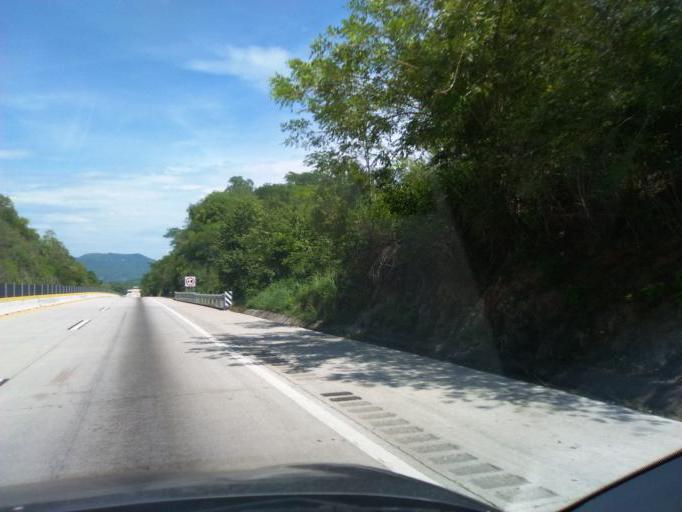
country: MX
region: Guerrero
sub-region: Acapulco de Juarez
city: Kilometro 30
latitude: 16.9636
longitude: -99.7360
